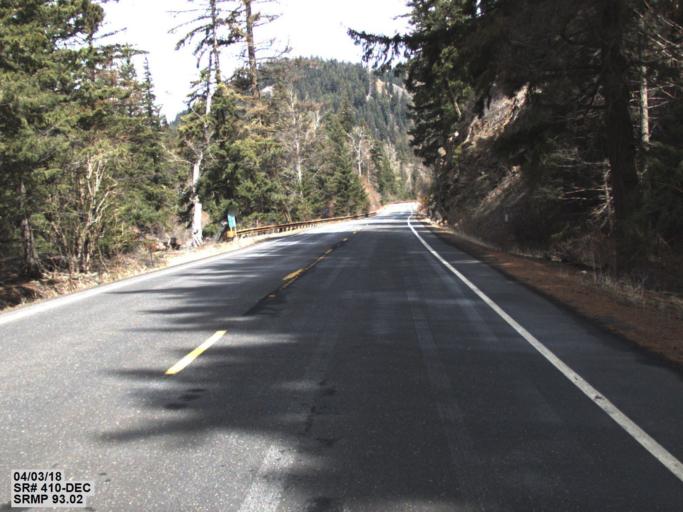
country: US
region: Washington
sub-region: Kittitas County
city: Cle Elum
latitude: 46.9790
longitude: -121.0944
